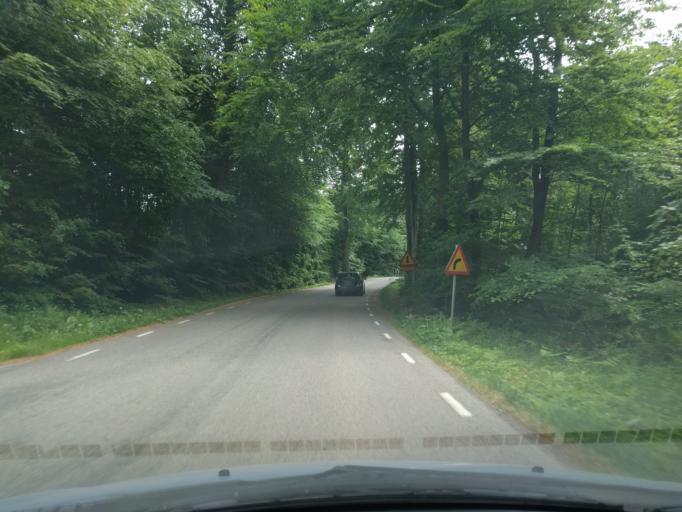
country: SE
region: Skane
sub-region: Svedala Kommun
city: Klagerup
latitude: 55.5593
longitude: 13.2146
